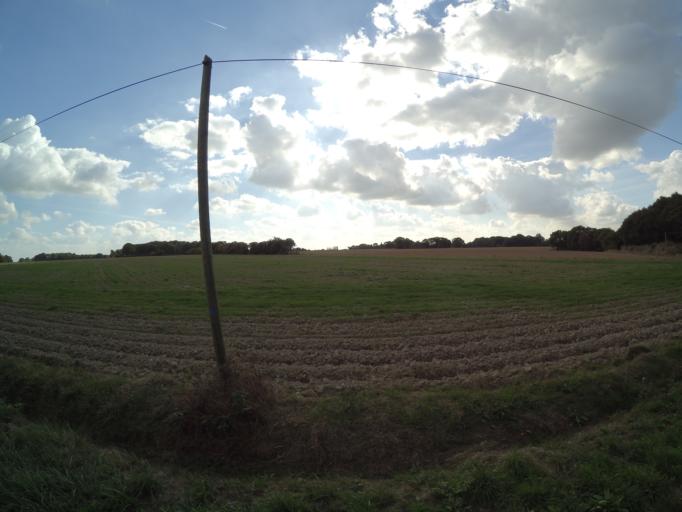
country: FR
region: Pays de la Loire
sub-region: Departement de la Loire-Atlantique
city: Remouille
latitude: 47.0727
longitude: -1.3666
